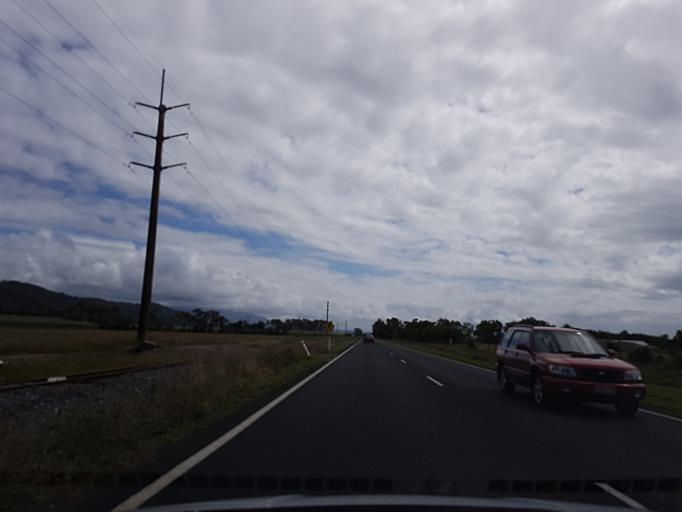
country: AU
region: Queensland
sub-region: Cairns
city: Port Douglas
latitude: -16.5125
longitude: 145.4444
